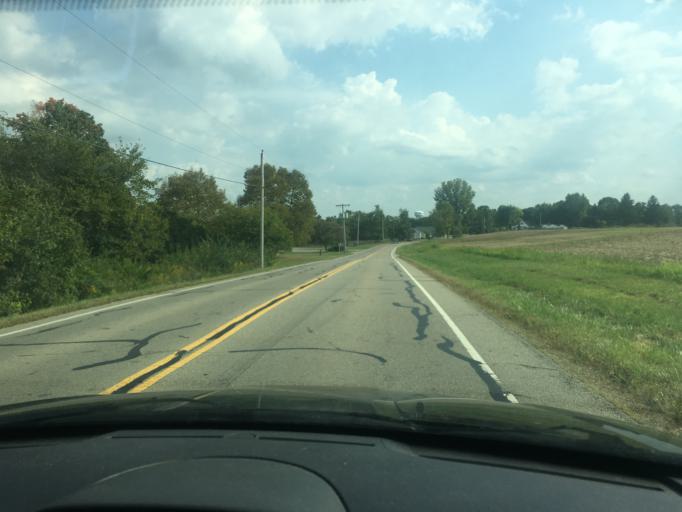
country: US
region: Ohio
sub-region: Champaign County
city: Urbana
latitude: 40.1218
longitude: -83.7660
